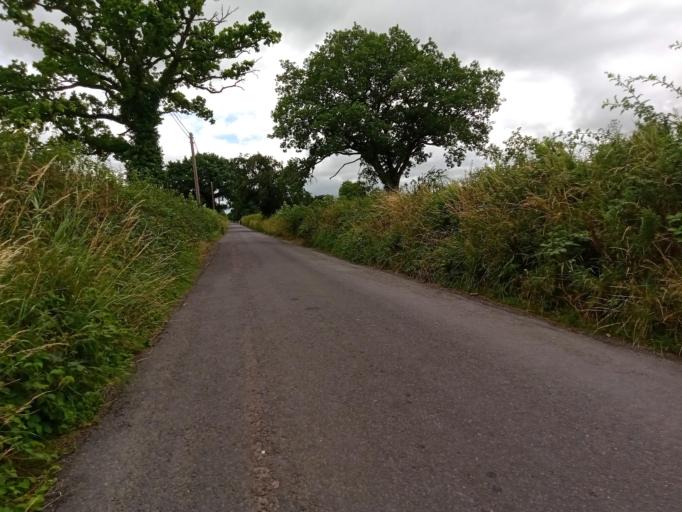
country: IE
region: Leinster
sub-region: Kilkenny
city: Callan
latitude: 52.5683
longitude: -7.3771
